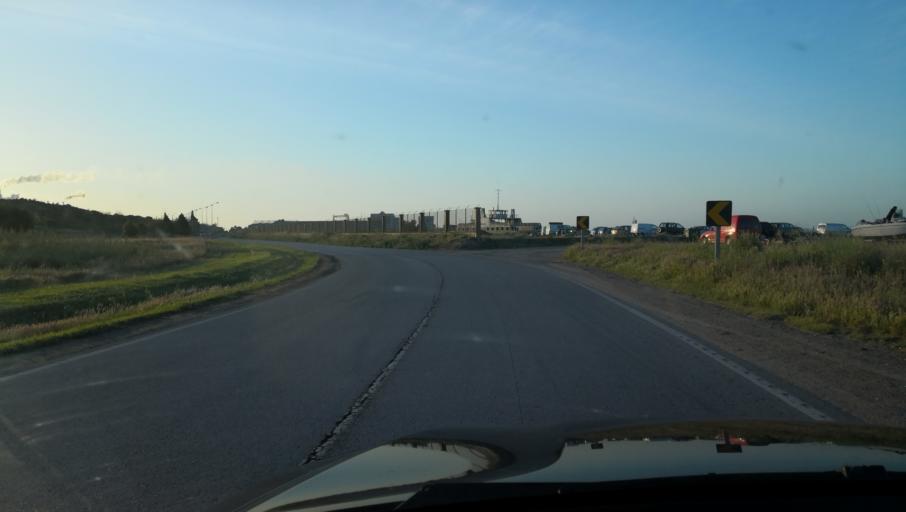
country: PT
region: Setubal
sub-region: Setubal
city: Setubal
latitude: 38.4941
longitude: -8.8319
